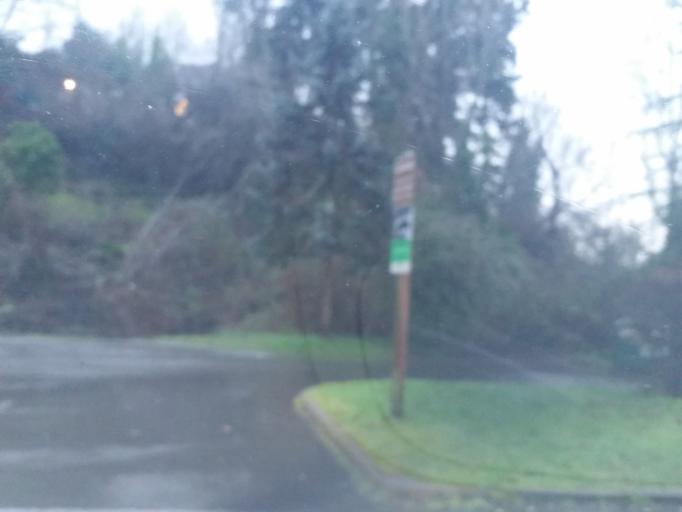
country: US
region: Washington
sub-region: Snohomish County
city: Meadowdale
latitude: 47.8802
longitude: -122.3320
